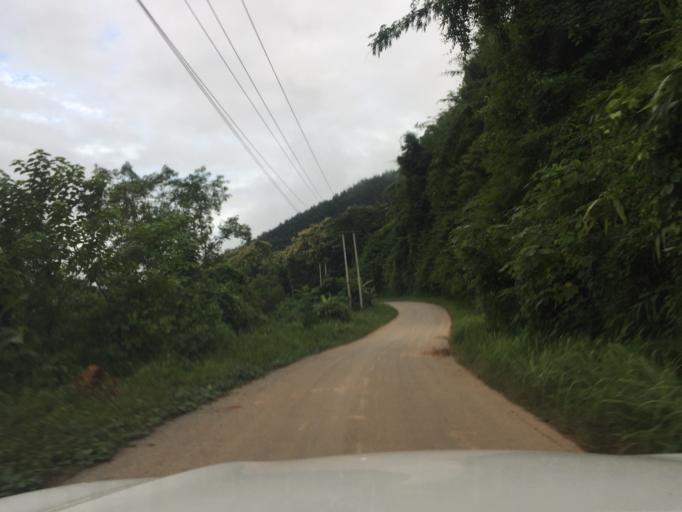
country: LA
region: Phongsali
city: Khoa
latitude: 21.0794
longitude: 102.3746
